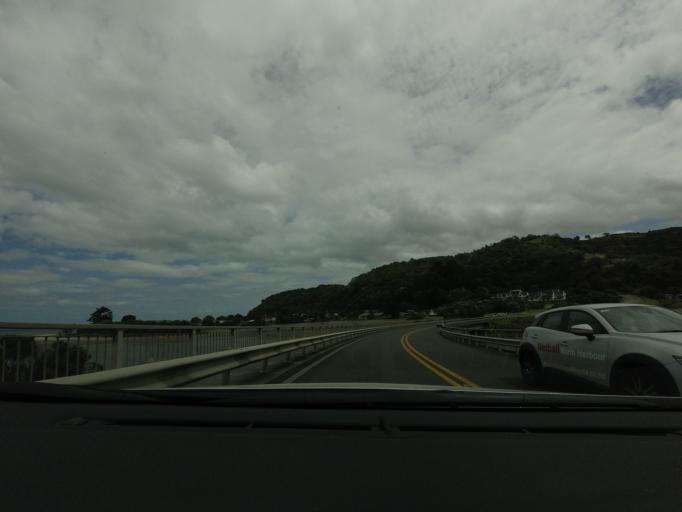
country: NZ
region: Auckland
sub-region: Auckland
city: Warkworth
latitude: -36.5408
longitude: 174.7057
